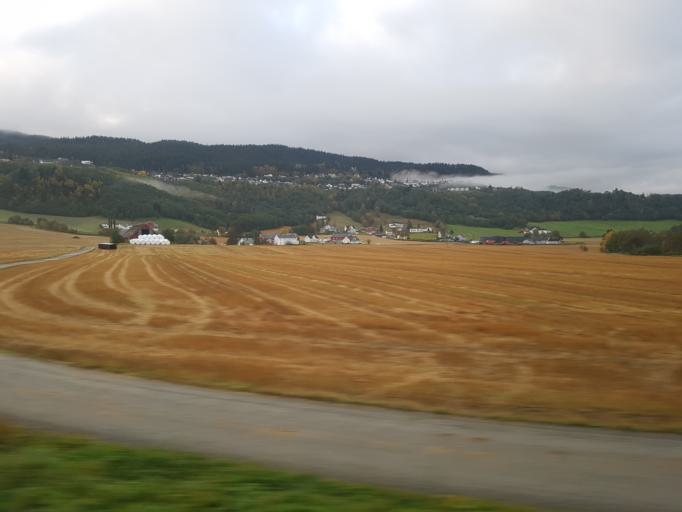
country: NO
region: Sor-Trondelag
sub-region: Melhus
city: Melhus
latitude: 63.3029
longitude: 10.2899
